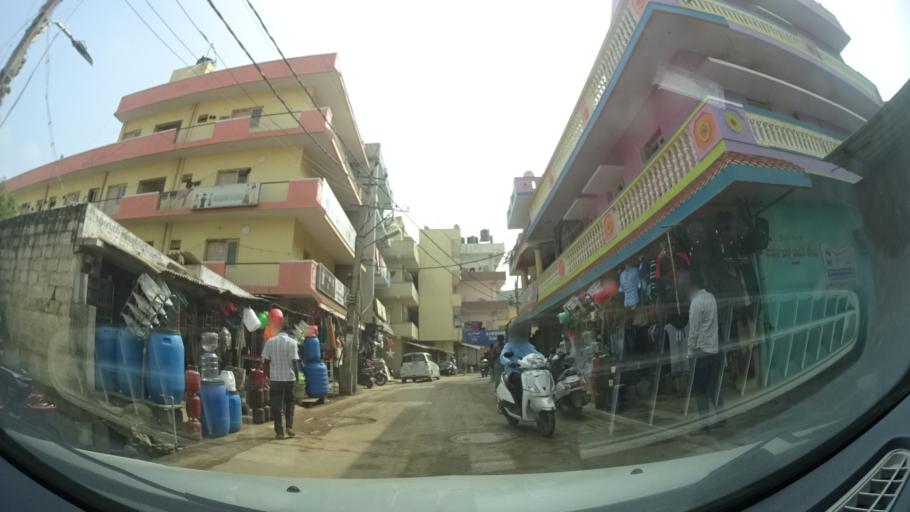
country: IN
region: Karnataka
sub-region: Bangalore Urban
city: Anekal
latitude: 12.8277
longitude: 77.6756
